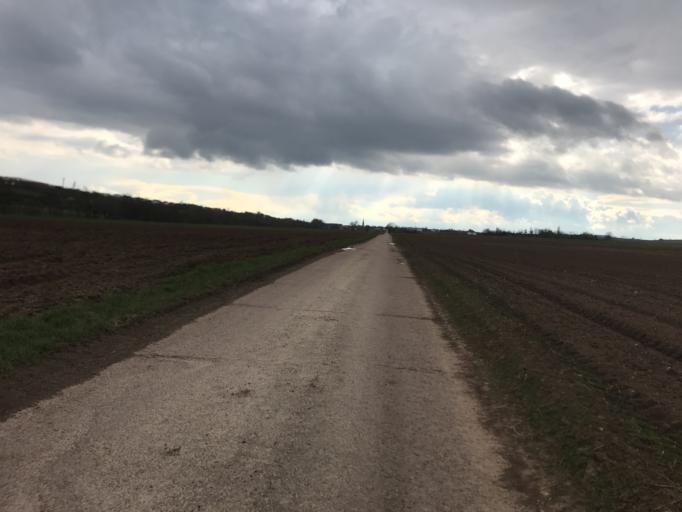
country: DE
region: Rheinland-Pfalz
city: Udenheim
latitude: 49.8905
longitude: 8.1729
